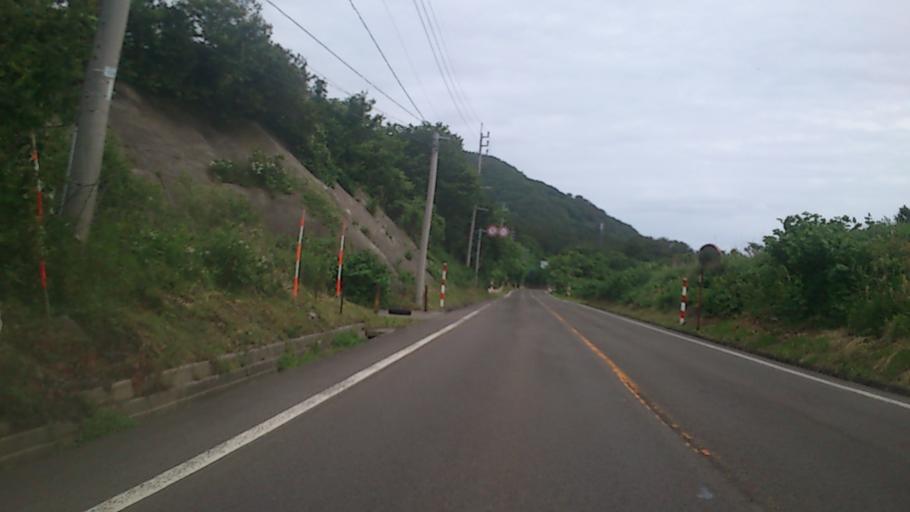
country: JP
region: Akita
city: Noshiromachi
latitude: 40.4257
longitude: 139.9437
